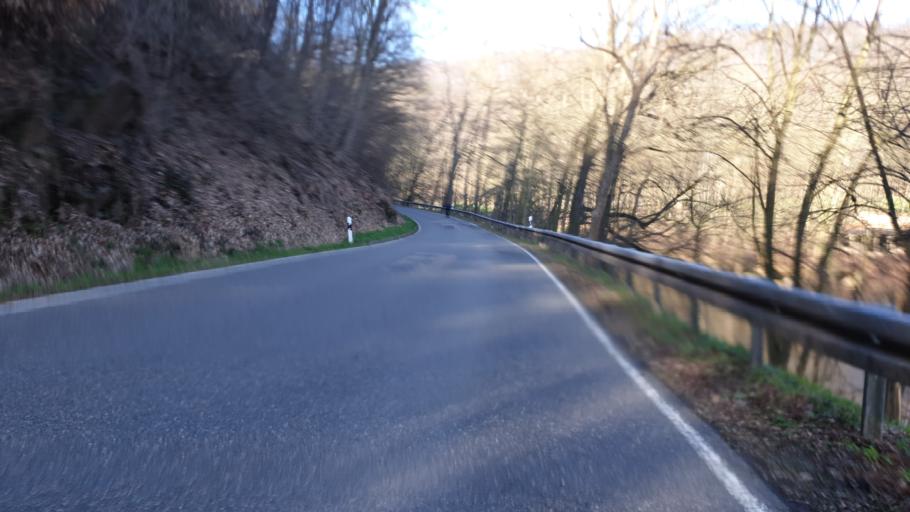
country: DE
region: Saxony
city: Taura
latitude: 50.9410
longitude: 12.8400
